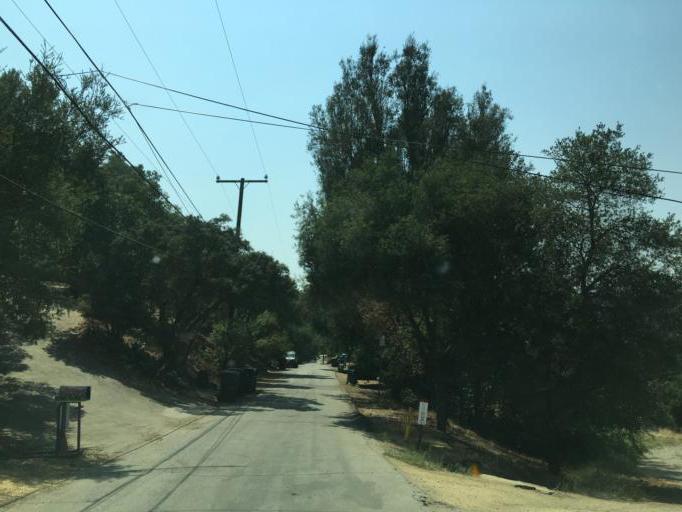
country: US
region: California
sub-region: Los Angeles County
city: Topanga
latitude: 34.1154
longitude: -118.5804
